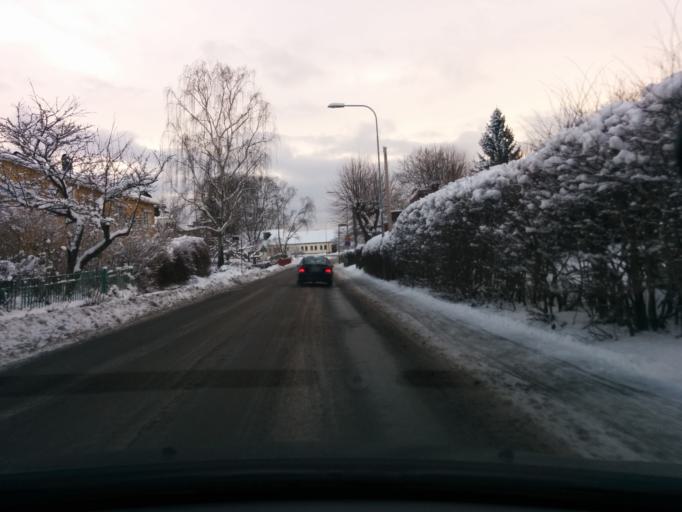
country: SE
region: Stockholm
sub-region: Stockholms Kommun
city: Arsta
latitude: 59.2842
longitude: 18.0237
